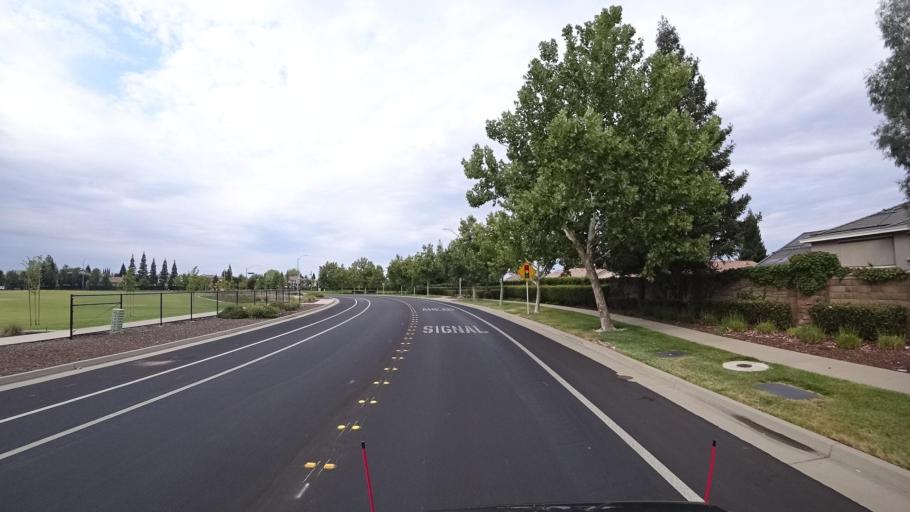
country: US
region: California
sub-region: Placer County
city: Rocklin
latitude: 38.7682
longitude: -121.2369
